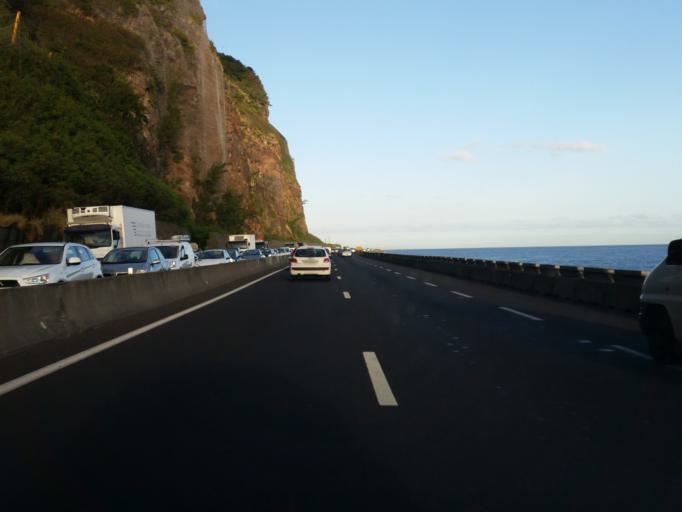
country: RE
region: Reunion
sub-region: Reunion
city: Saint-Denis
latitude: -20.8806
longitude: 55.3998
